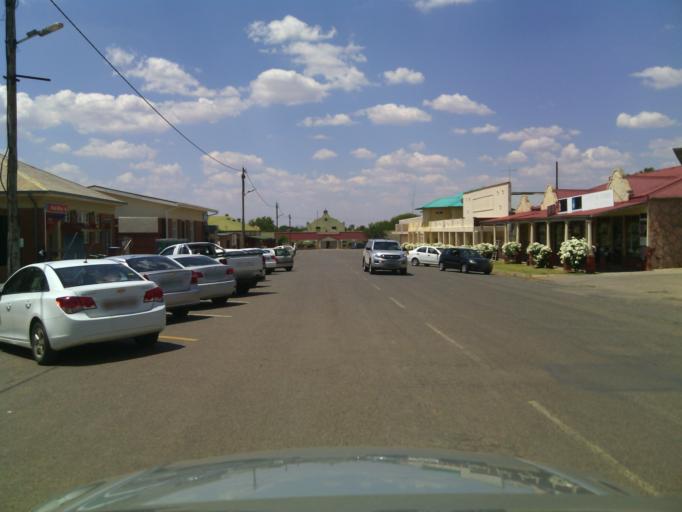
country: ZA
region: Orange Free State
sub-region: Xhariep District Municipality
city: Dewetsdorp
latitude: -29.5845
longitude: 26.6625
